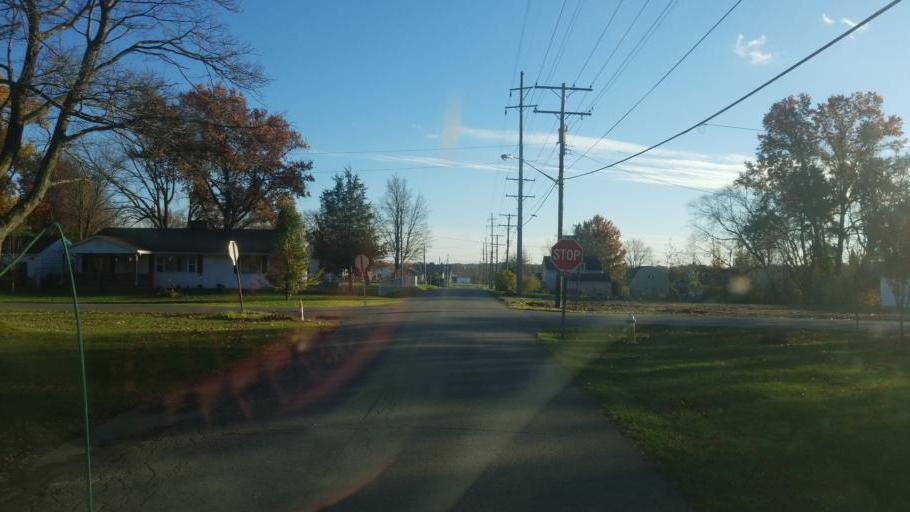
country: US
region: Ohio
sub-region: Richland County
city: Ontario
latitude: 40.7788
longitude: -82.5559
